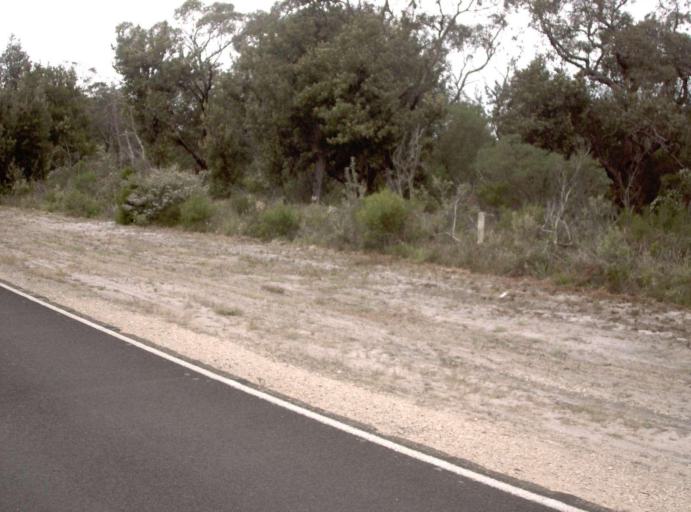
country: AU
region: Victoria
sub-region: East Gippsland
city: Bairnsdale
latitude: -38.0660
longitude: 147.5557
